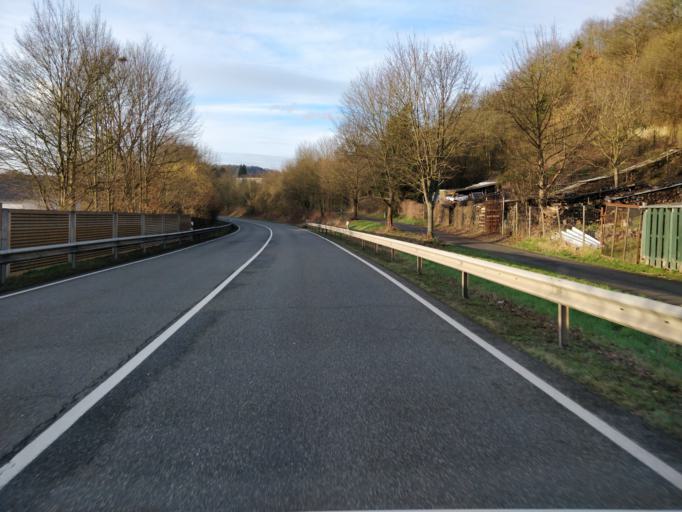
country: DE
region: Rheinland-Pfalz
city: Rheinbrohl
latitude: 50.5044
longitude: 7.3308
